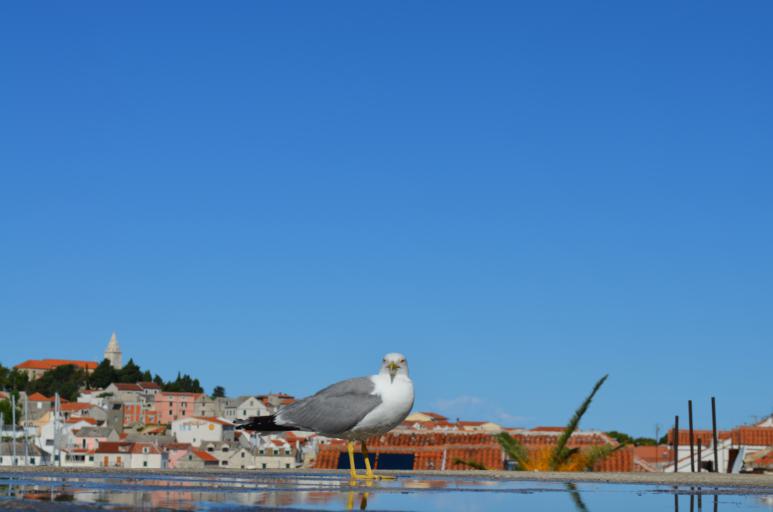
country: HR
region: Sibensko-Kniniska
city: Primosten
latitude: 43.5876
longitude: 15.9240
